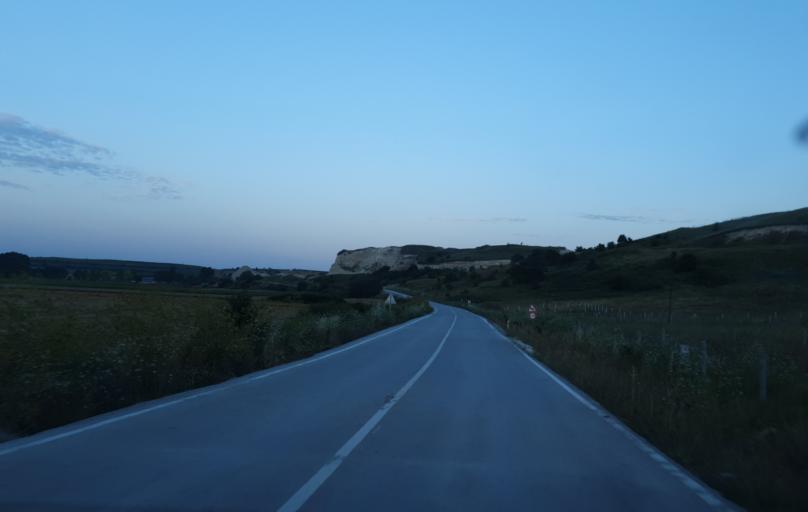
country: TR
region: Tekirdag
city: Velimese
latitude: 41.3489
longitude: 27.8600
